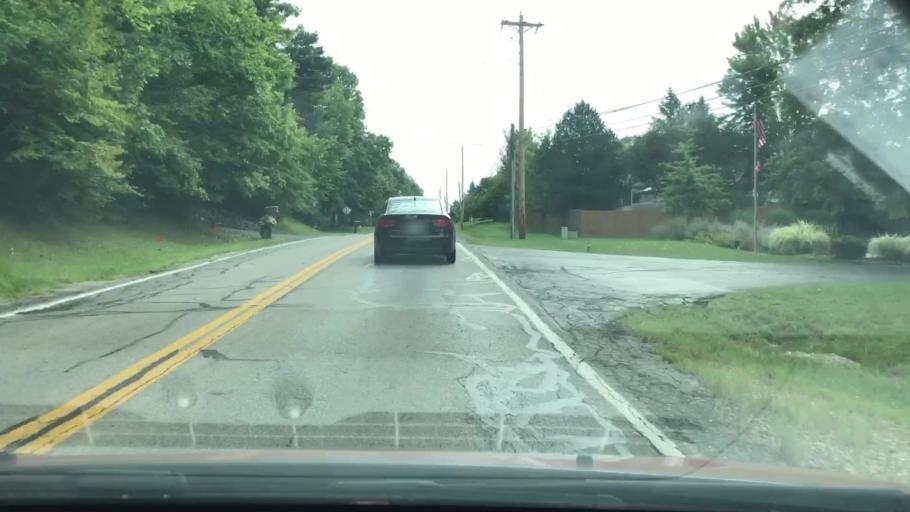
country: US
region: Ohio
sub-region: Franklin County
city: Huber Ridge
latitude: 40.0945
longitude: -82.9011
